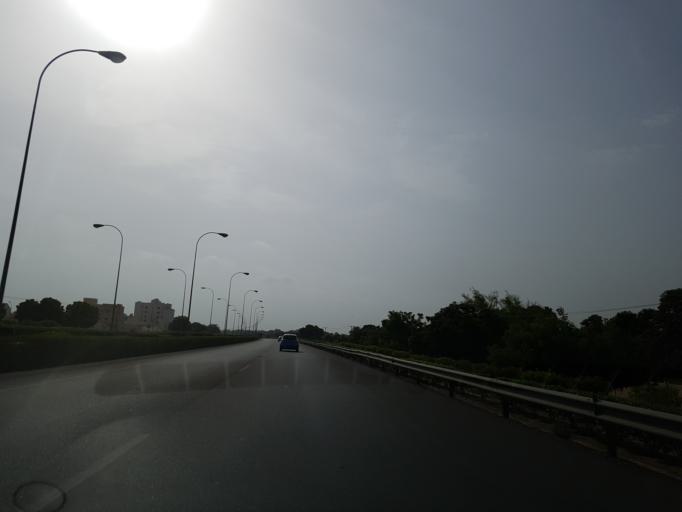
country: OM
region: Al Batinah
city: Al Sohar
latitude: 24.3971
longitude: 56.6708
